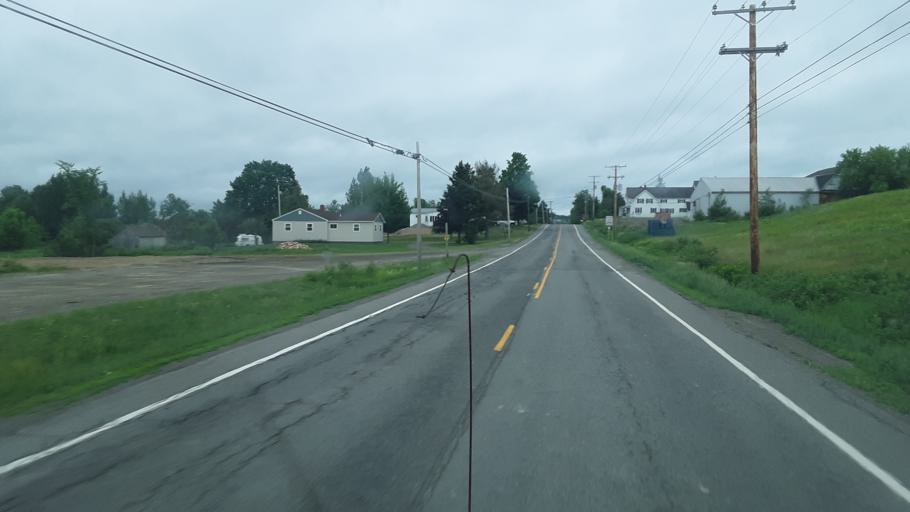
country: US
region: Maine
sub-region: Penobscot County
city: Patten
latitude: 46.0077
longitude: -68.4465
